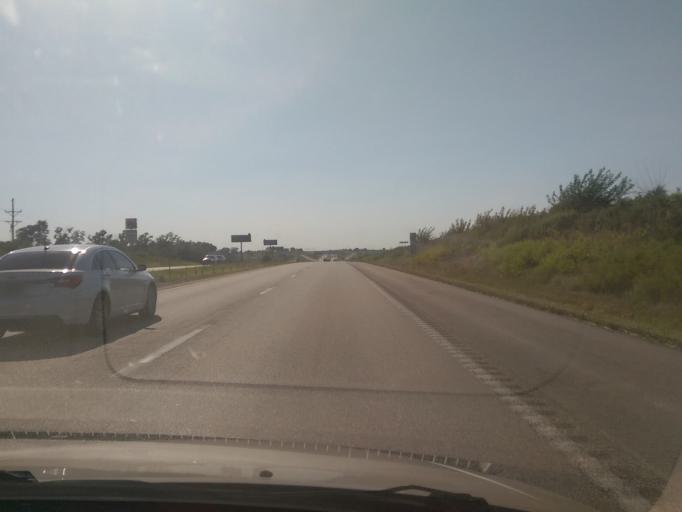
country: US
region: Missouri
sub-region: Saline County
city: Sweet Springs
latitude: 38.9817
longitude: -93.4791
